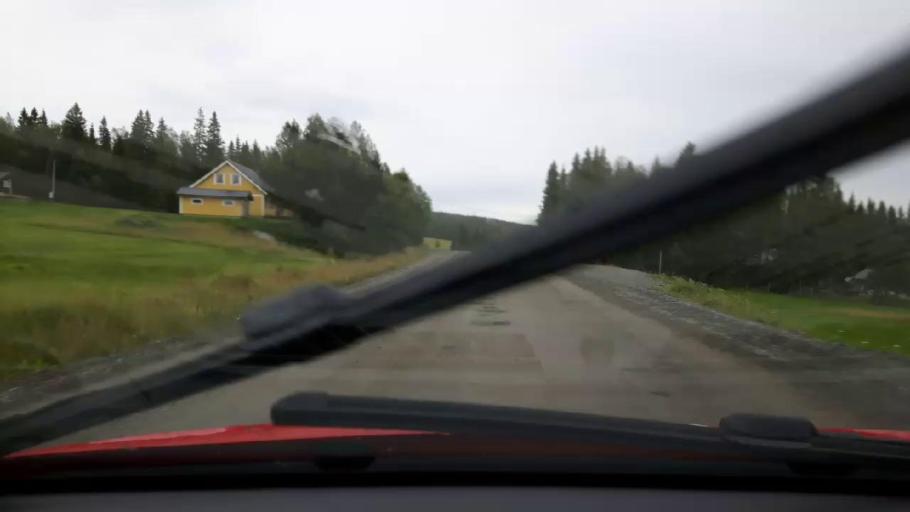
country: SE
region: Jaemtland
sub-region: Are Kommun
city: Are
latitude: 63.4639
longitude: 12.6234
